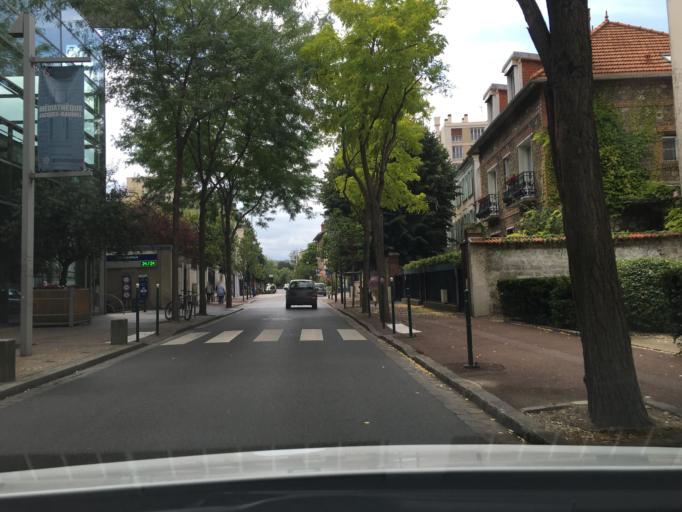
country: FR
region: Ile-de-France
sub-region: Departement des Hauts-de-Seine
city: Rueil-Malmaison
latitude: 48.8780
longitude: 2.1799
